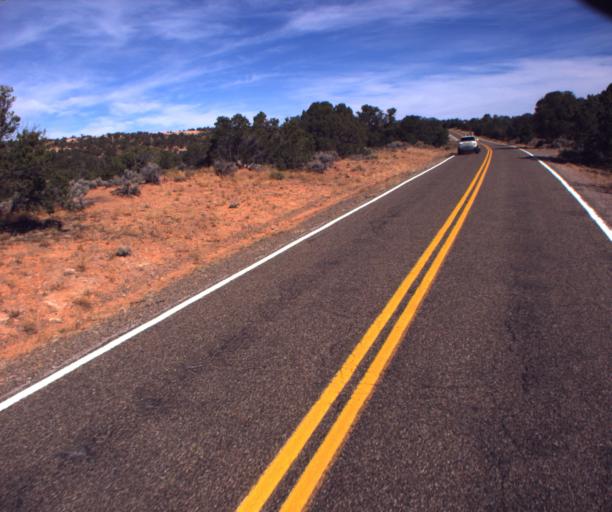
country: US
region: Arizona
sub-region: Navajo County
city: Kayenta
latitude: 36.5761
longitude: -110.4927
